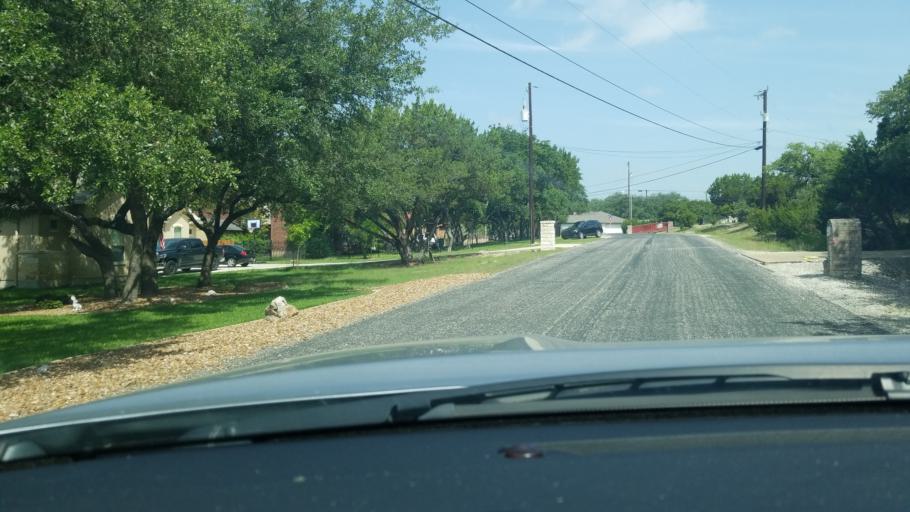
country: US
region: Texas
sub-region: Bexar County
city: Timberwood Park
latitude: 29.6920
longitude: -98.4944
